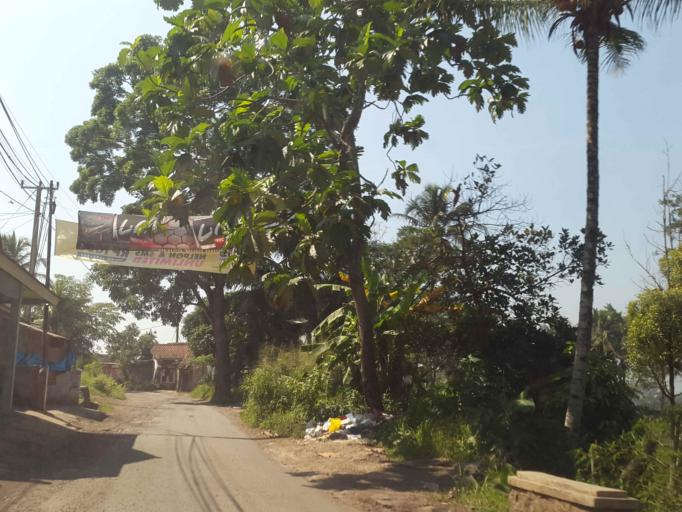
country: ID
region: West Java
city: Ciranjang-hilir
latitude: -6.8447
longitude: 107.1120
